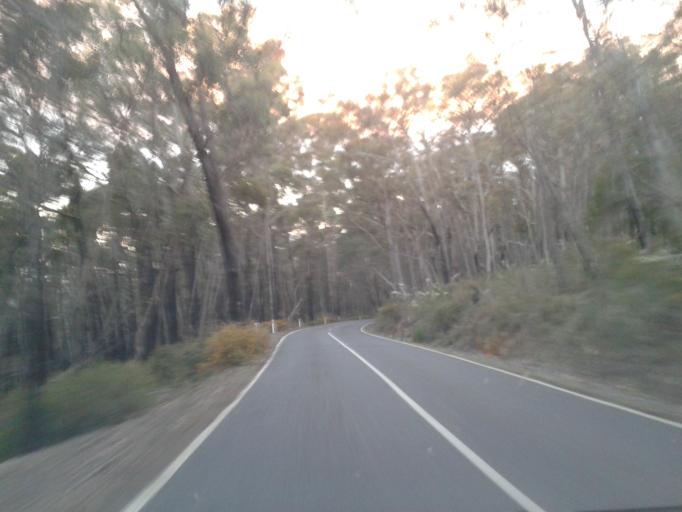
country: AU
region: Victoria
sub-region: Northern Grampians
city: Stawell
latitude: -37.1539
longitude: 142.4880
